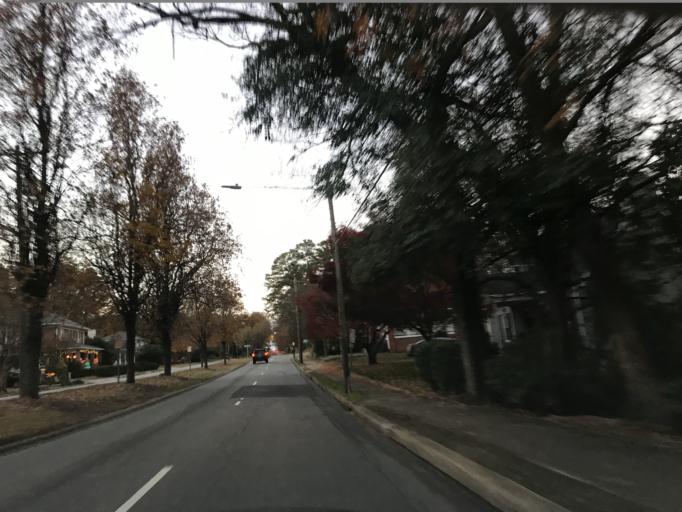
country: US
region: North Carolina
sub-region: Wake County
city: West Raleigh
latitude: 35.8071
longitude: -78.6476
